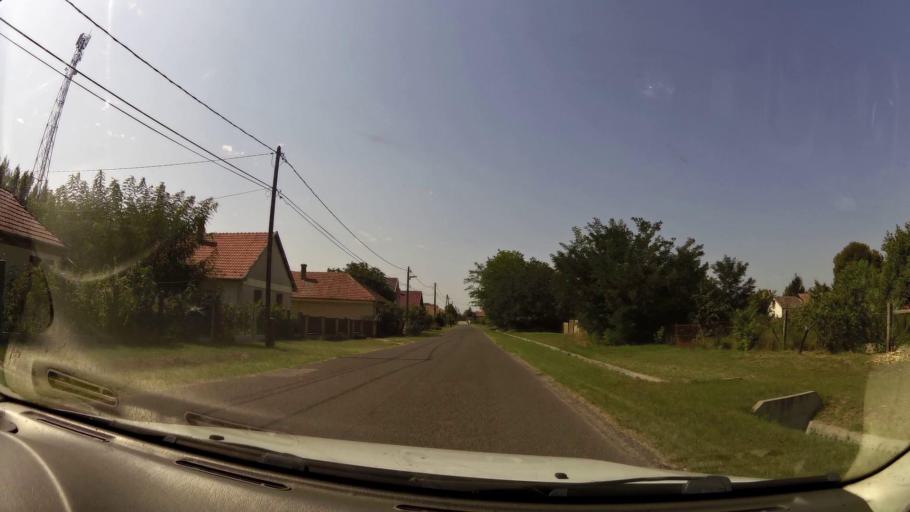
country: HU
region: Pest
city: Ujszilvas
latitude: 47.2741
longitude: 19.9259
